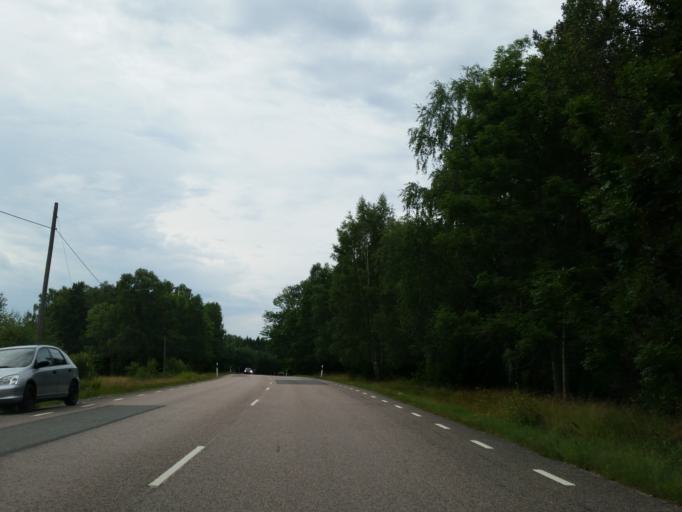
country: SE
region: Stockholm
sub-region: Nykvarns Kommun
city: Nykvarn
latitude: 59.1923
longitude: 17.5250
